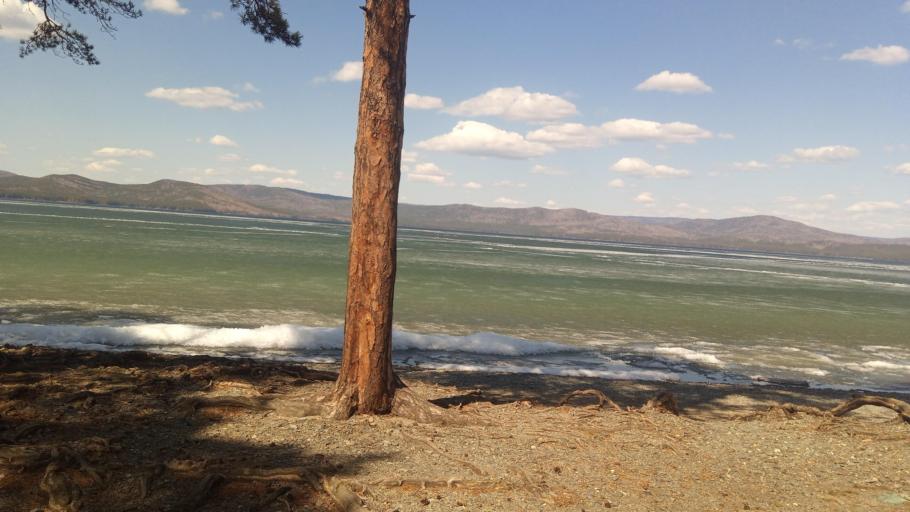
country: RU
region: Chelyabinsk
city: Turgoyak
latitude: 55.1520
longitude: 60.1093
